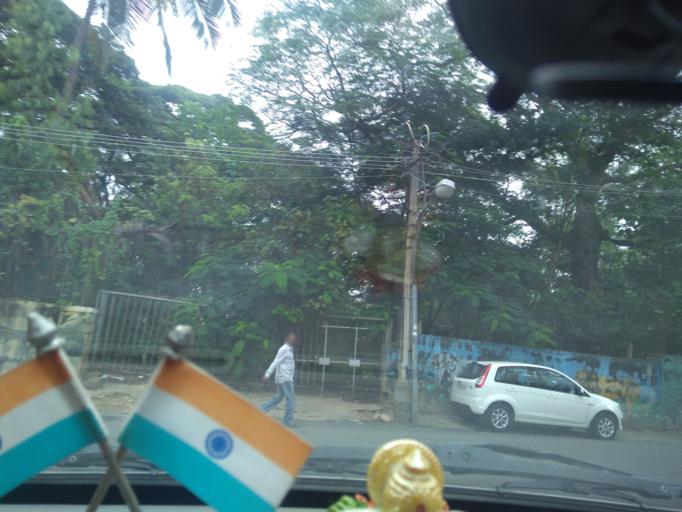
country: IN
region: Karnataka
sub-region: Bangalore Urban
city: Bangalore
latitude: 12.9886
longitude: 77.5518
